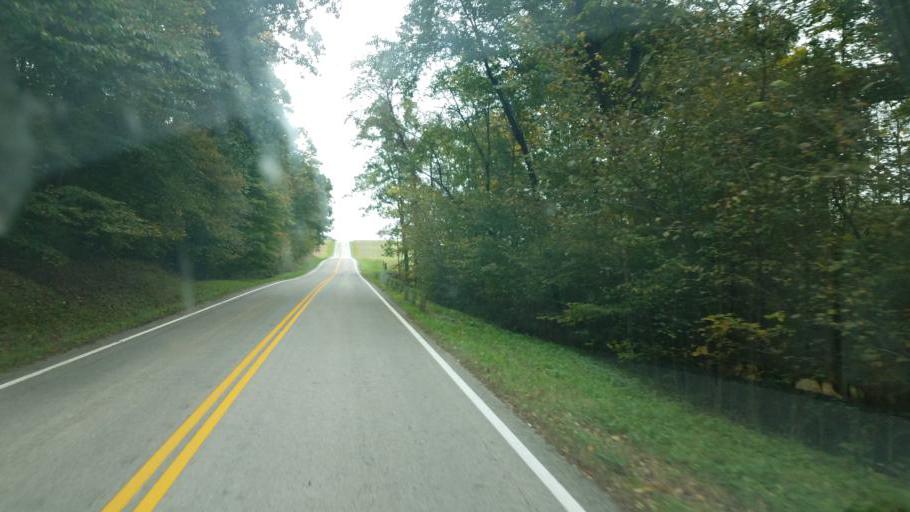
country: US
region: Ohio
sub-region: Ashland County
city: Loudonville
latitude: 40.6369
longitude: -82.2977
